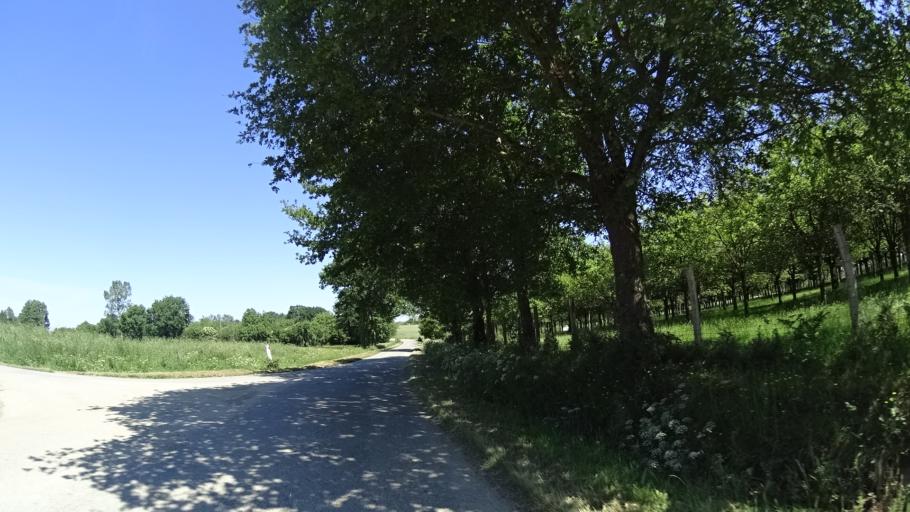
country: FR
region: Brittany
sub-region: Departement d'Ille-et-Vilaine
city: Messac
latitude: 47.7913
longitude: -1.8112
